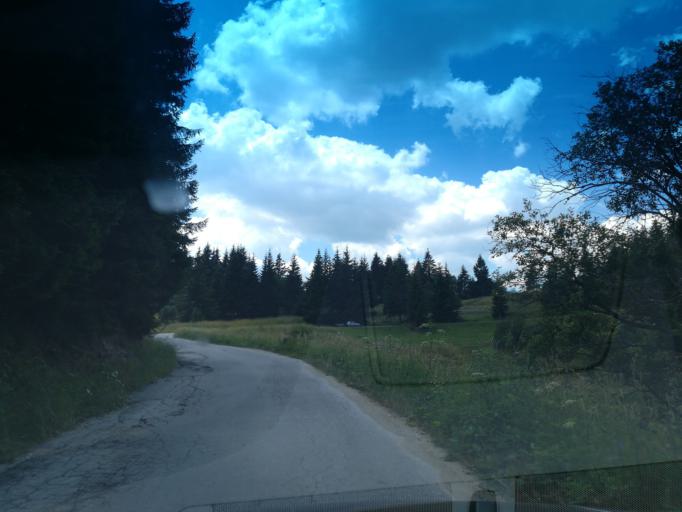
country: BG
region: Smolyan
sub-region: Obshtina Chepelare
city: Chepelare
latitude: 41.6765
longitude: 24.7717
